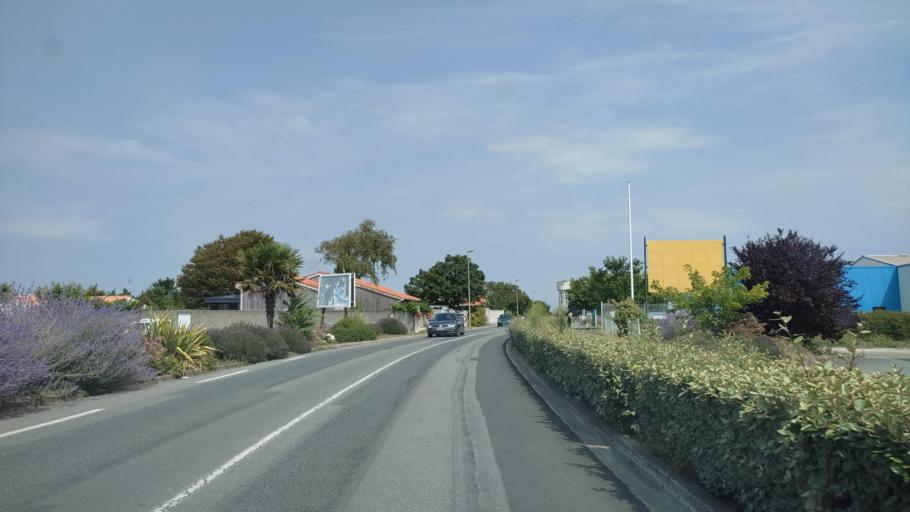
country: FR
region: Poitou-Charentes
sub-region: Departement de la Charente-Maritime
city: Chatelaillon-Plage
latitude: 46.0837
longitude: -1.0735
